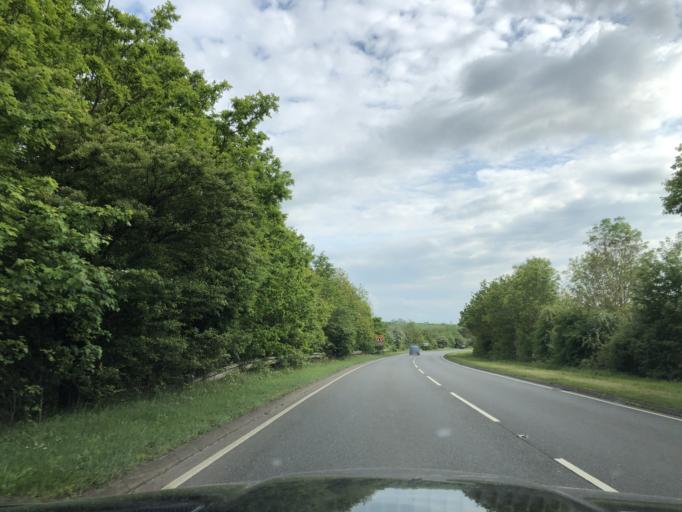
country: GB
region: England
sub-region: Warwickshire
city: Wellesbourne Mountford
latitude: 52.1335
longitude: -1.6139
